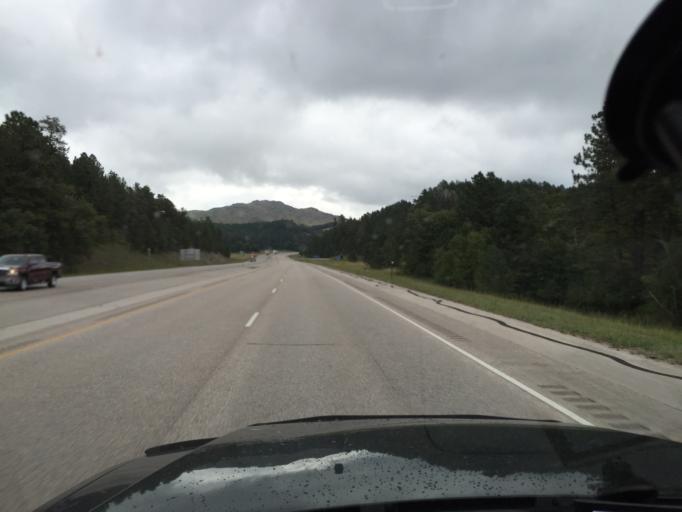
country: US
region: South Dakota
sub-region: Pennington County
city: Colonial Pine Hills
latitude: 43.9273
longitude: -103.4322
